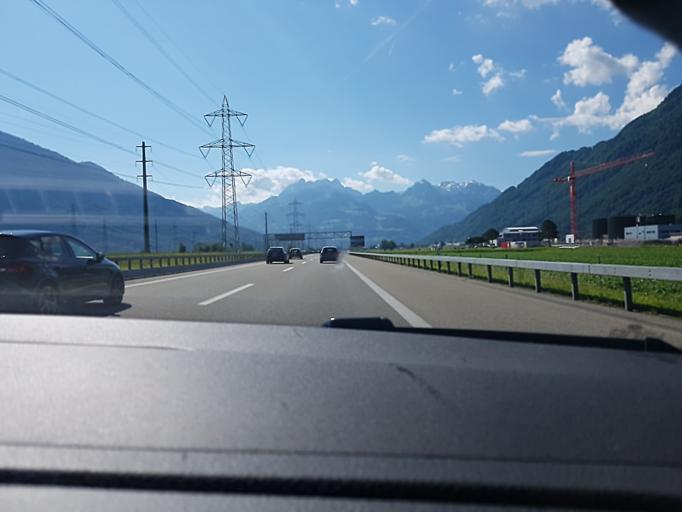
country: CH
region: Glarus
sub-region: Glarus
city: Bilten
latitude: 47.1681
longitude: 9.0121
